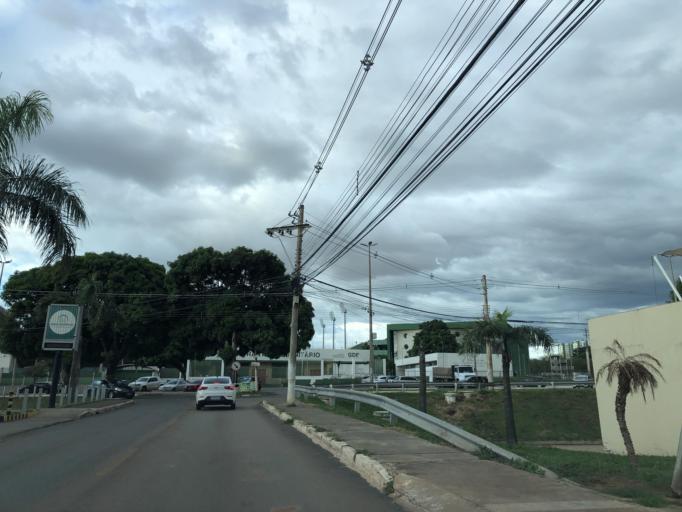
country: BR
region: Goias
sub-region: Luziania
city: Luziania
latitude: -16.0141
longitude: -48.0617
